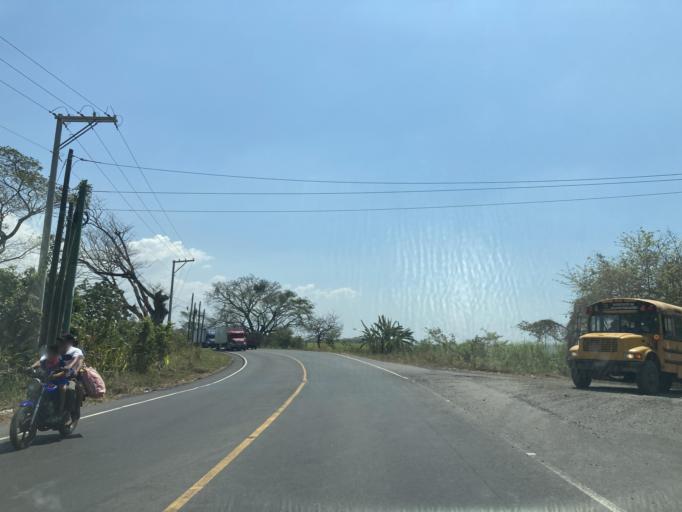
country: GT
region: Escuintla
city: Guanagazapa
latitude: 14.1019
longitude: -90.6169
